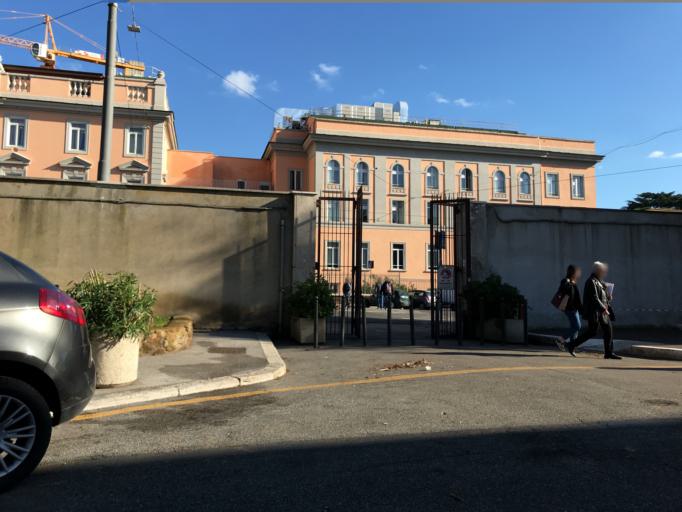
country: IT
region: Latium
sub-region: Citta metropolitana di Roma Capitale
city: Rome
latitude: 41.9048
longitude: 12.5163
